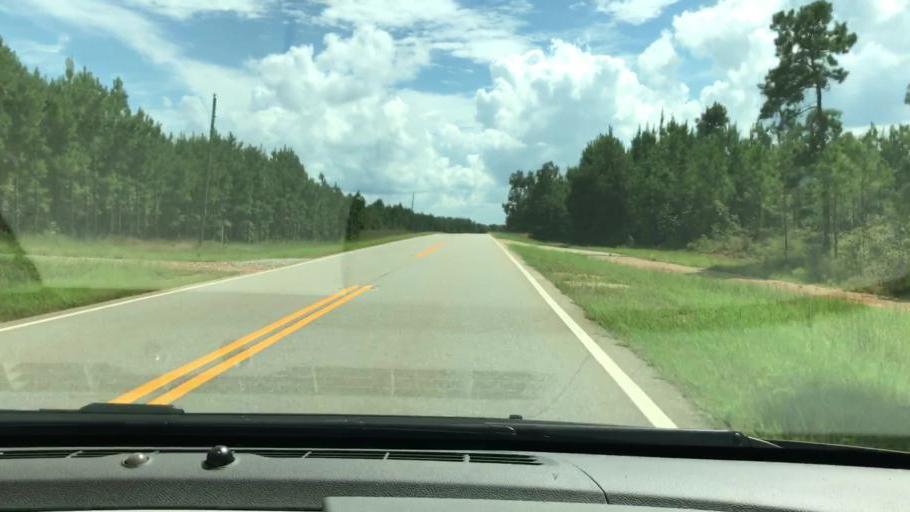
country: US
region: Georgia
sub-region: Quitman County
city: Georgetown
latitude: 31.9187
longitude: -85.0594
